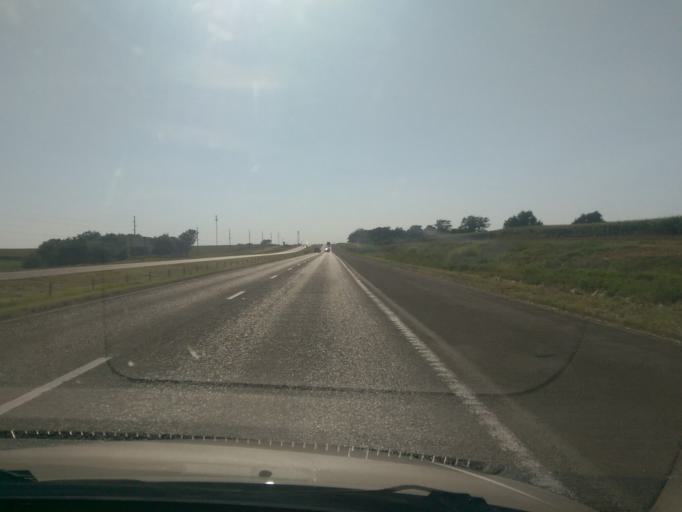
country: US
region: Missouri
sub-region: Lafayette County
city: Concordia
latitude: 38.9920
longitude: -93.6565
